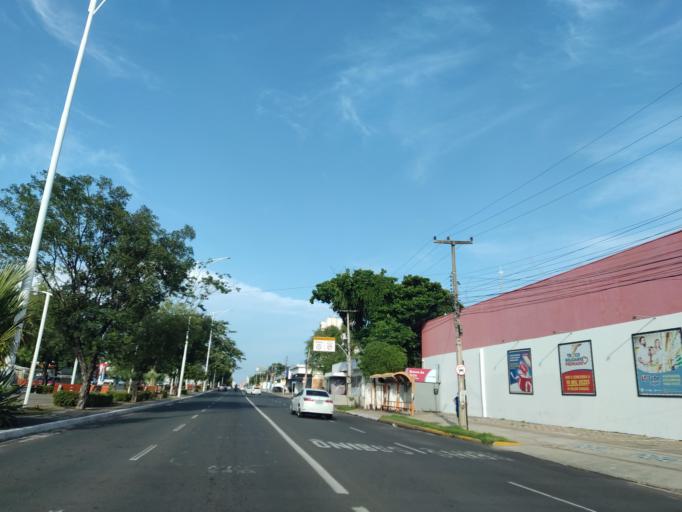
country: BR
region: Piaui
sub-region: Teresina
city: Teresina
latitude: -5.0860
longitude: -42.8017
